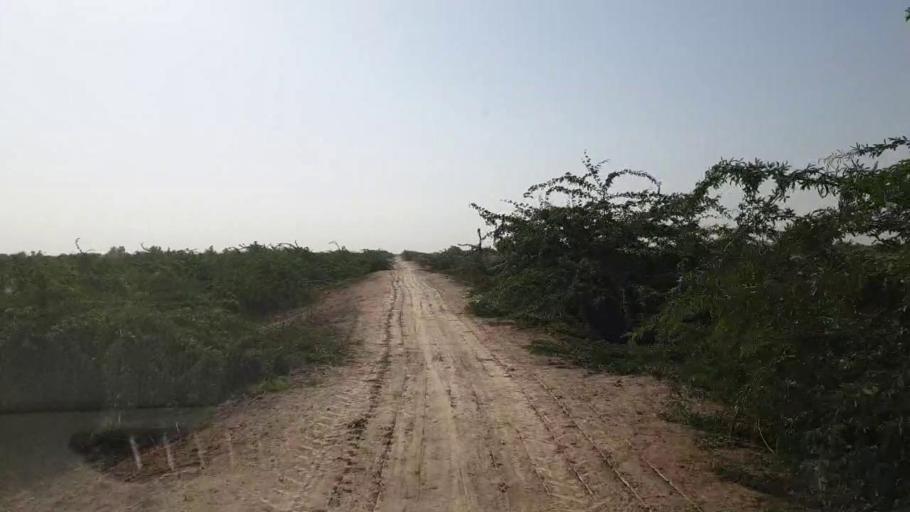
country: PK
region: Sindh
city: Kadhan
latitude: 24.5790
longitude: 69.0802
